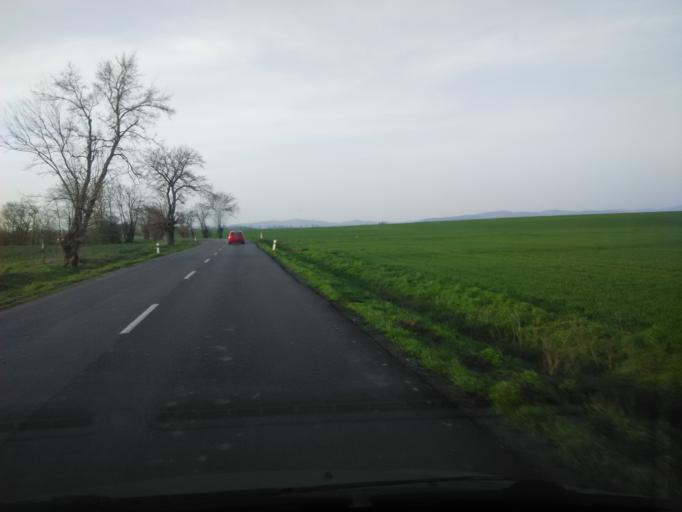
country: SK
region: Nitriansky
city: Tlmace
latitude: 48.1625
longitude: 18.4517
